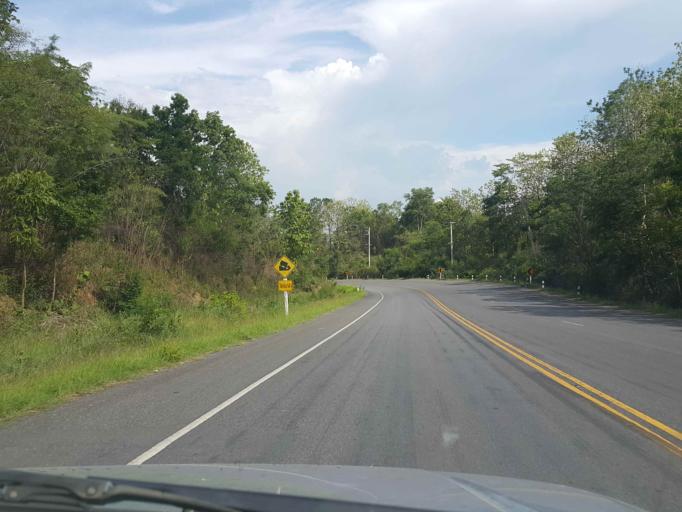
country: TH
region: Lampang
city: Wang Nuea
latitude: 19.1539
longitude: 99.5897
